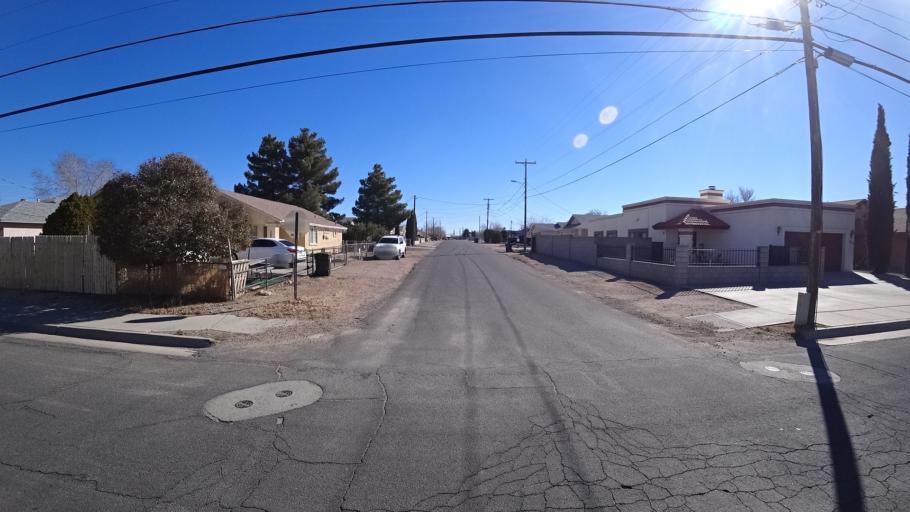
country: US
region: Arizona
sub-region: Mohave County
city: Kingman
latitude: 35.2053
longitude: -114.0291
